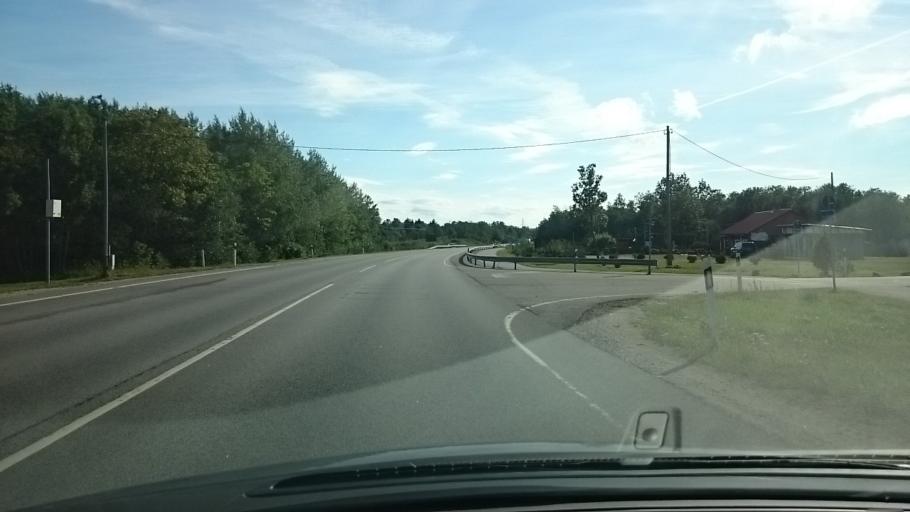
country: EE
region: Laeaene
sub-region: Ridala Parish
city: Uuemoisa
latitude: 58.9525
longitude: 23.6588
